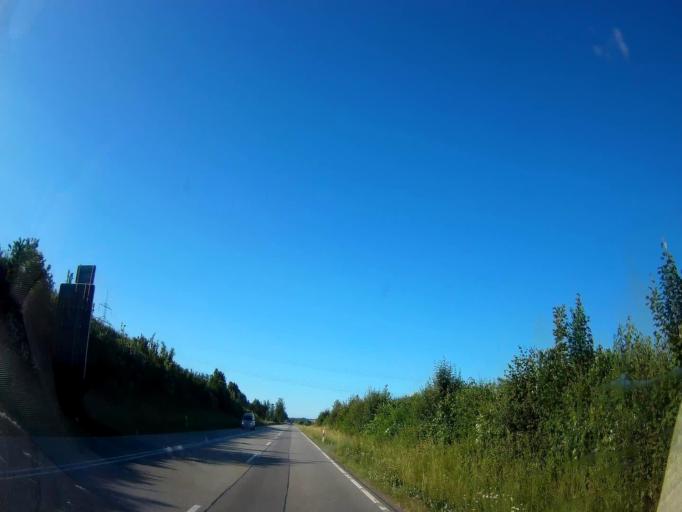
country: DE
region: Bavaria
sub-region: Lower Bavaria
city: Parkstetten
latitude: 48.9185
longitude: 12.6187
